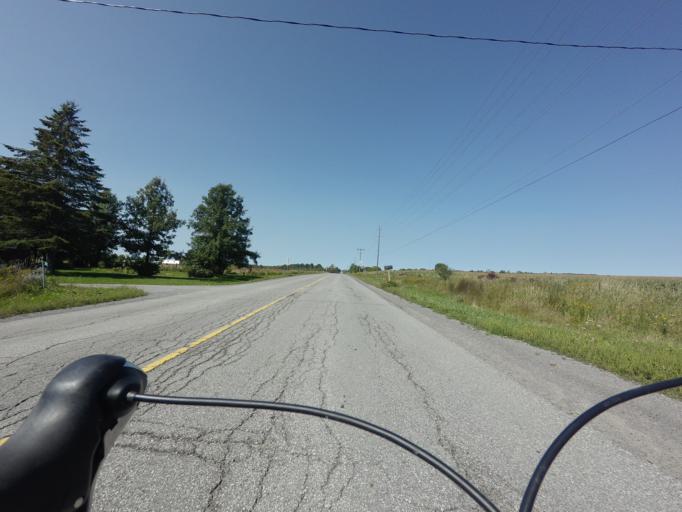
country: CA
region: Ontario
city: Arnprior
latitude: 45.4562
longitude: -76.0917
